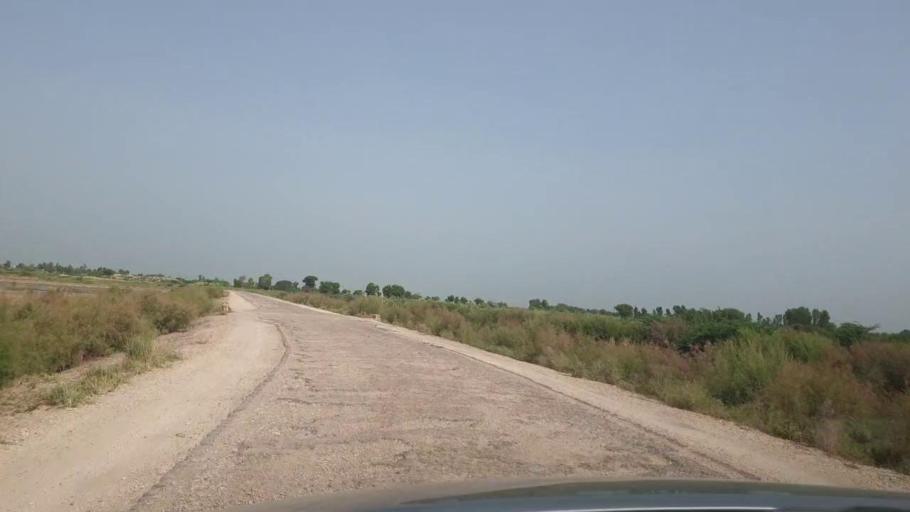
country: PK
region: Sindh
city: Madeji
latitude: 27.8381
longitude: 68.4425
